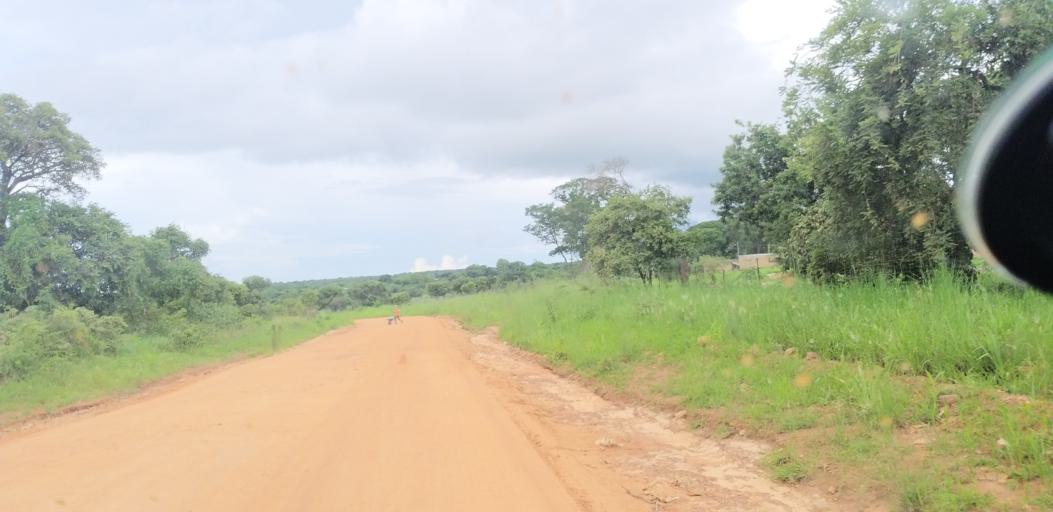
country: ZM
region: Lusaka
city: Lusaka
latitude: -15.1973
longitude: 28.4419
